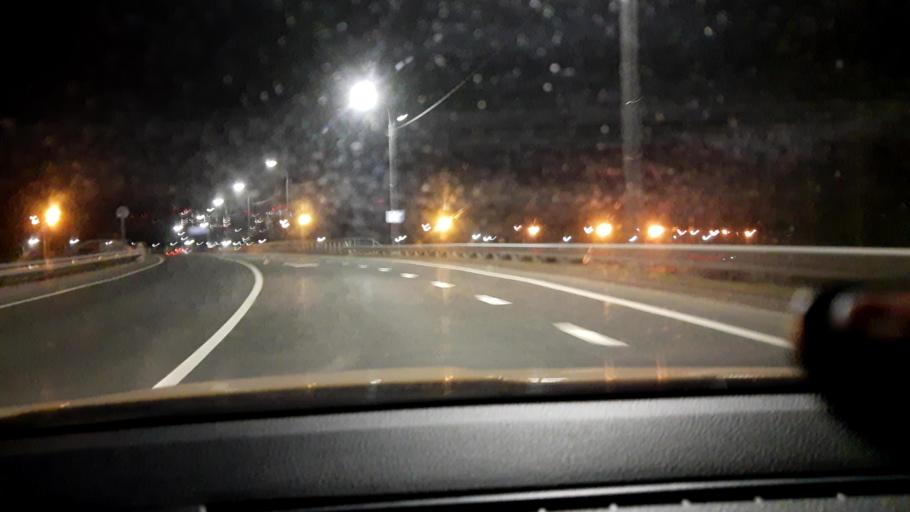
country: RU
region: Moskovskaya
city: Krasnoznamensk
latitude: 55.6101
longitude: 37.0544
